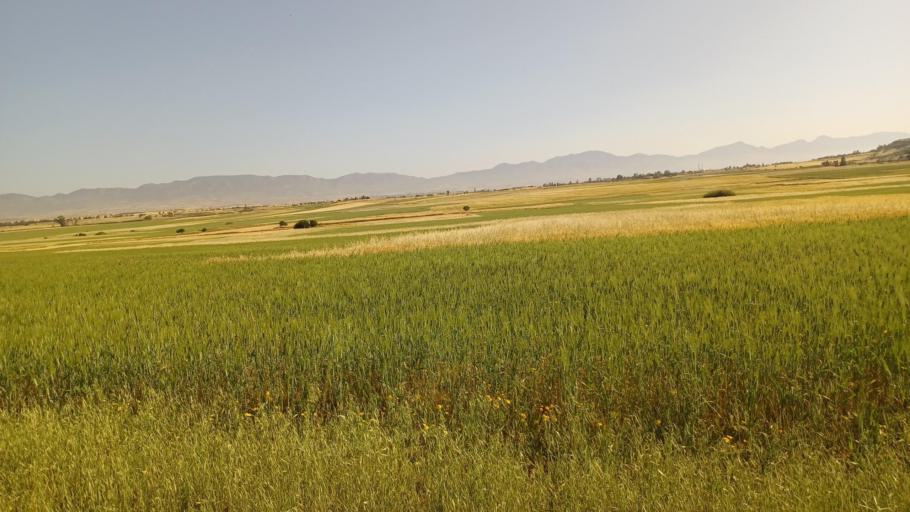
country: CY
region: Lefkosia
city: Mammari
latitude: 35.1642
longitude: 33.2388
